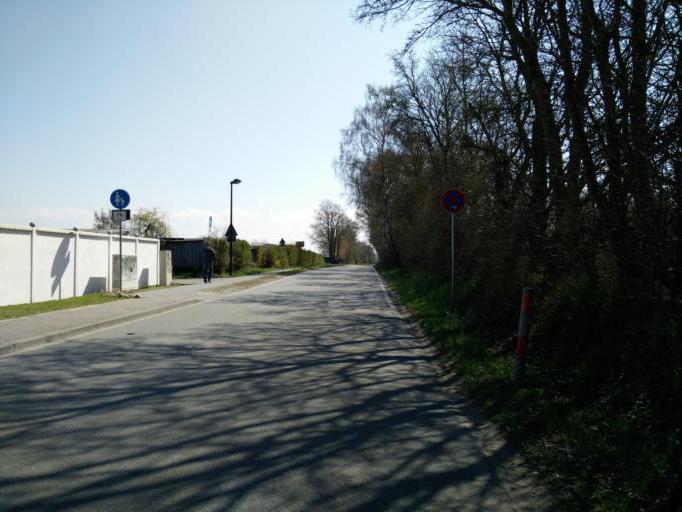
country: DE
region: Mecklenburg-Vorpommern
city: Elmenhorst
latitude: 54.1350
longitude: 12.0328
